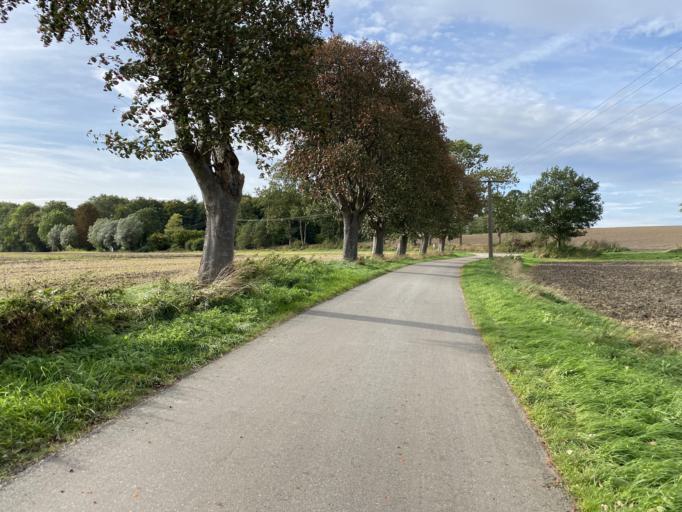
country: DE
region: Schleswig-Holstein
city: Grube
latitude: 54.2578
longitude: 11.0449
